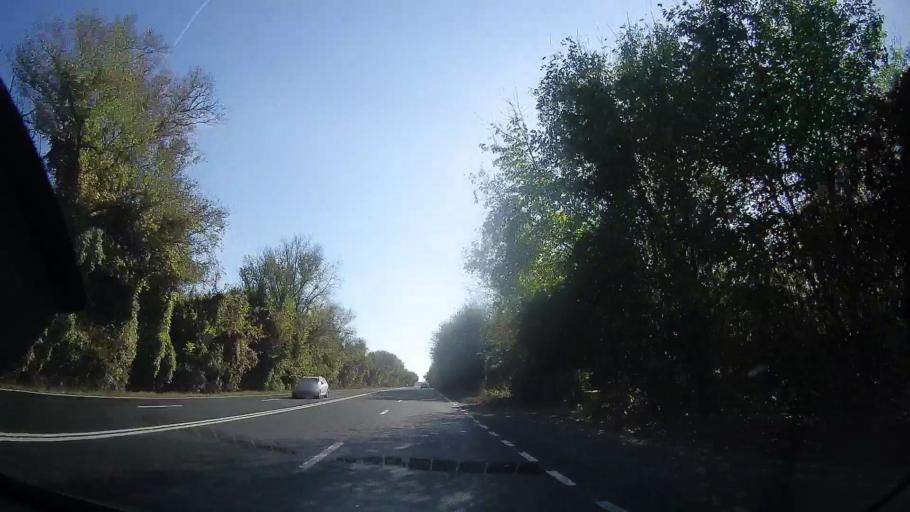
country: RO
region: Constanta
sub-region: Comuna Douazeci si Trei August
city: Dulcesti
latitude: 43.8661
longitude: 28.5750
